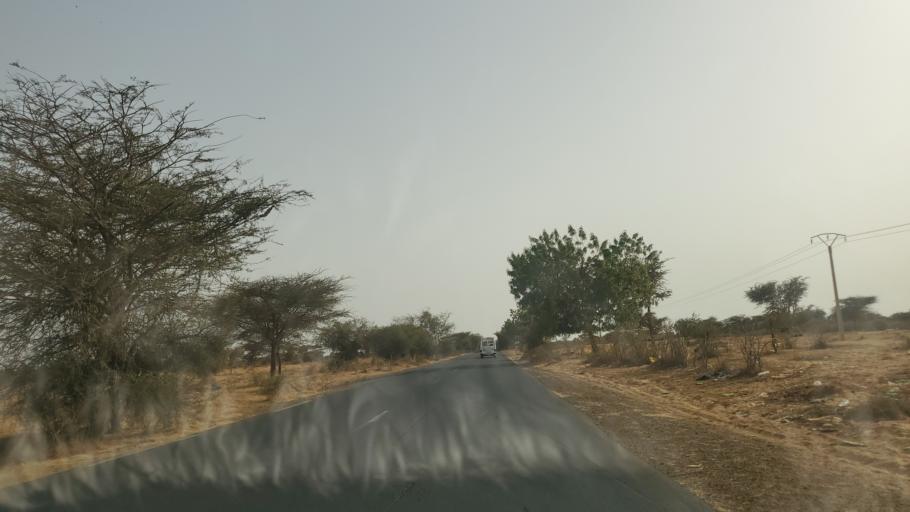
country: SN
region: Louga
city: Gueoul
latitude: 15.4551
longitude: -16.3726
